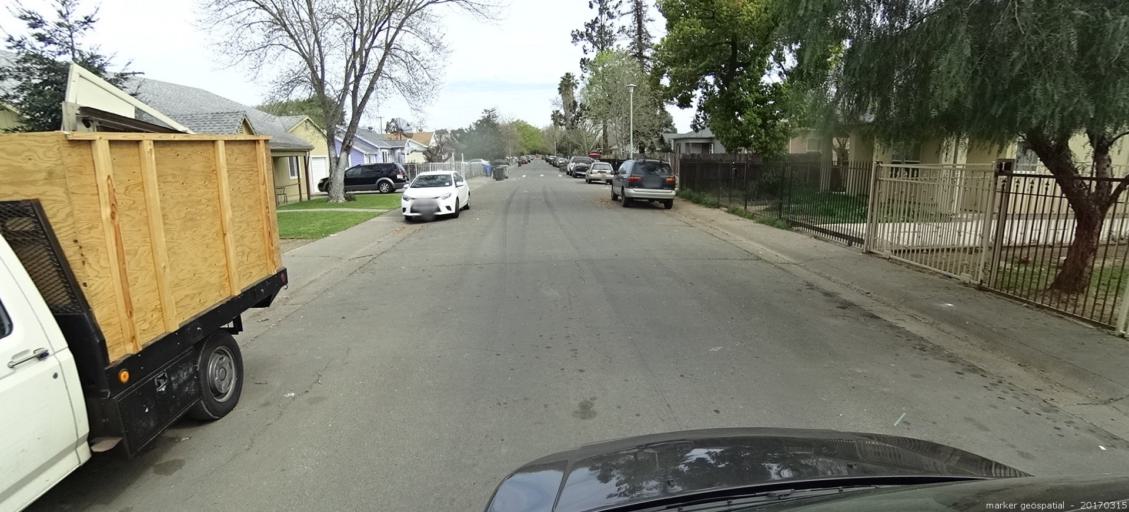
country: US
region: California
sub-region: Sacramento County
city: Parkway
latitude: 38.5209
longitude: -121.4769
